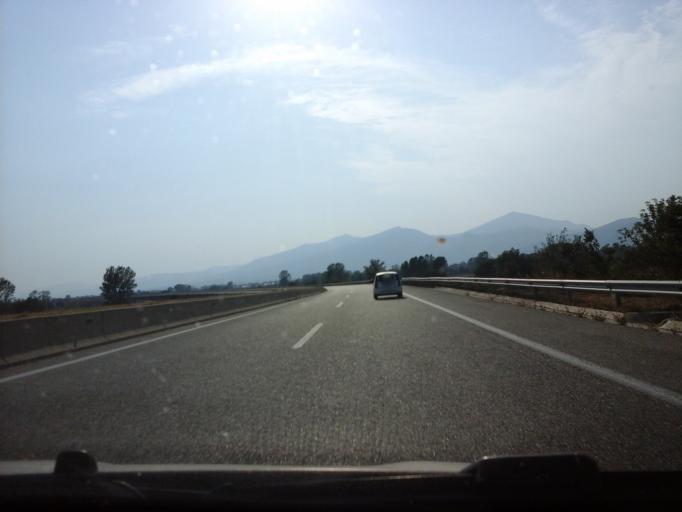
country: GR
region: East Macedonia and Thrace
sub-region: Nomos Xanthis
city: Selero
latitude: 41.1187
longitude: 24.9942
